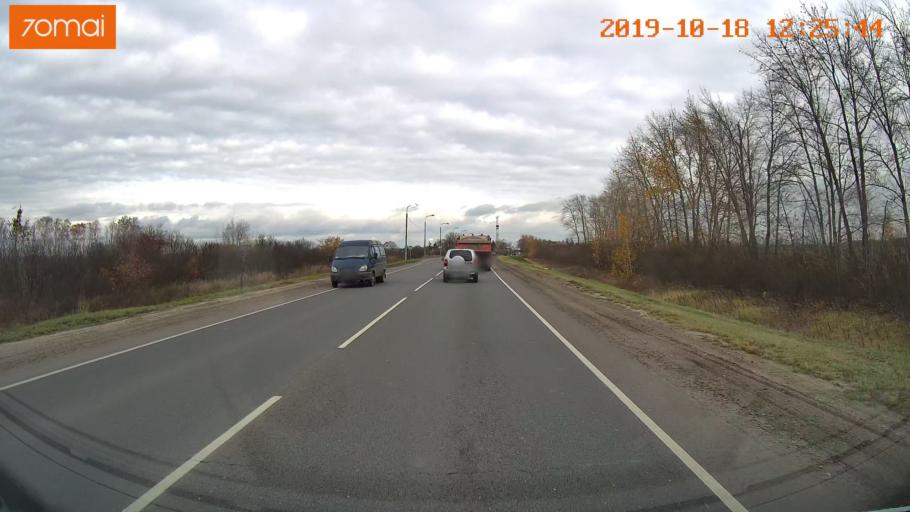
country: RU
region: Rjazan
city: Rybnoye
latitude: 54.5528
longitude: 39.5237
